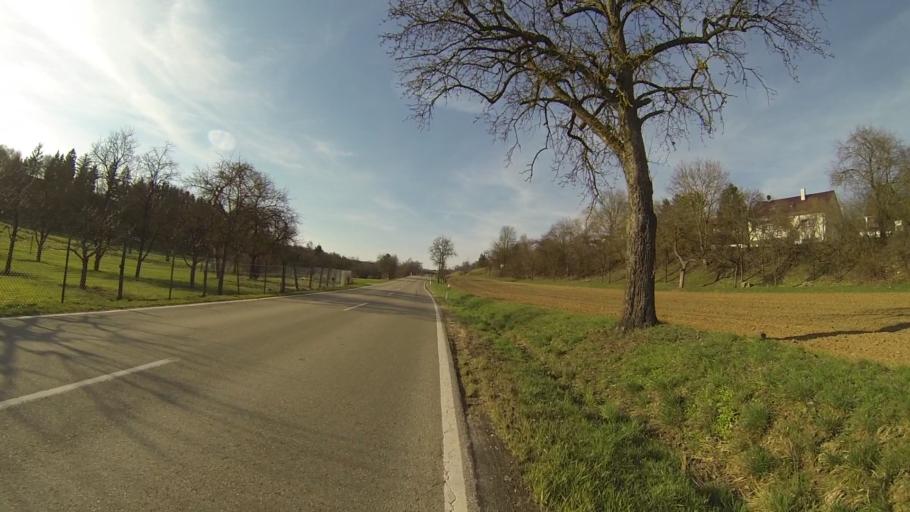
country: DE
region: Baden-Wuerttemberg
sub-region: Regierungsbezirk Stuttgart
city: Herbrechtingen
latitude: 48.5998
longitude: 10.2028
